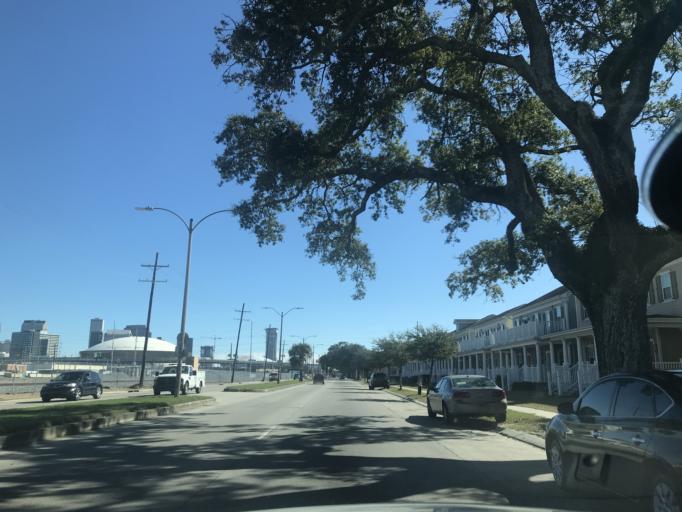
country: US
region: Louisiana
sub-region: Orleans Parish
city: New Orleans
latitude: 29.9537
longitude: -90.0941
